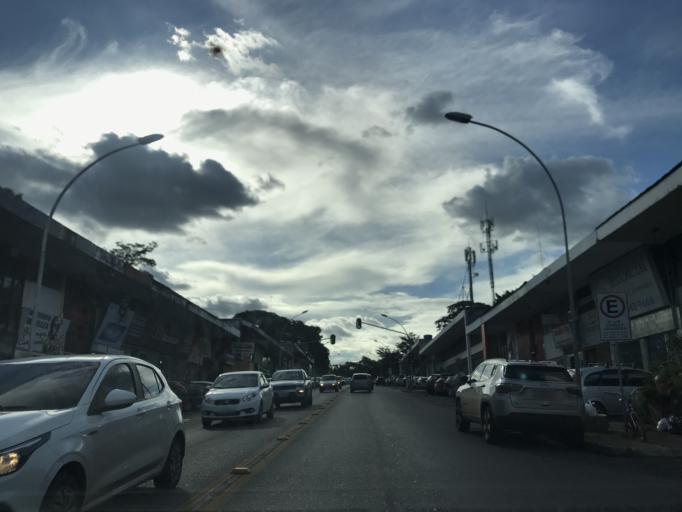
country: BR
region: Federal District
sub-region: Brasilia
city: Brasilia
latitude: -15.8193
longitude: -47.8951
